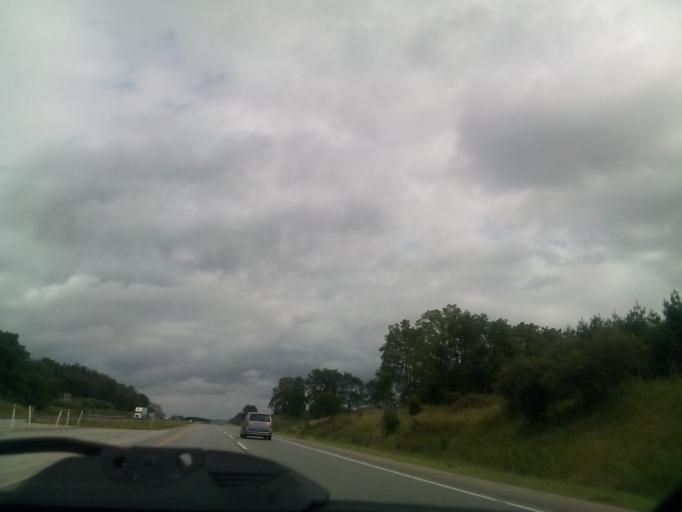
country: US
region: Indiana
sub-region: Steuben County
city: Fremont
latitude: 41.7076
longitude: -84.9333
